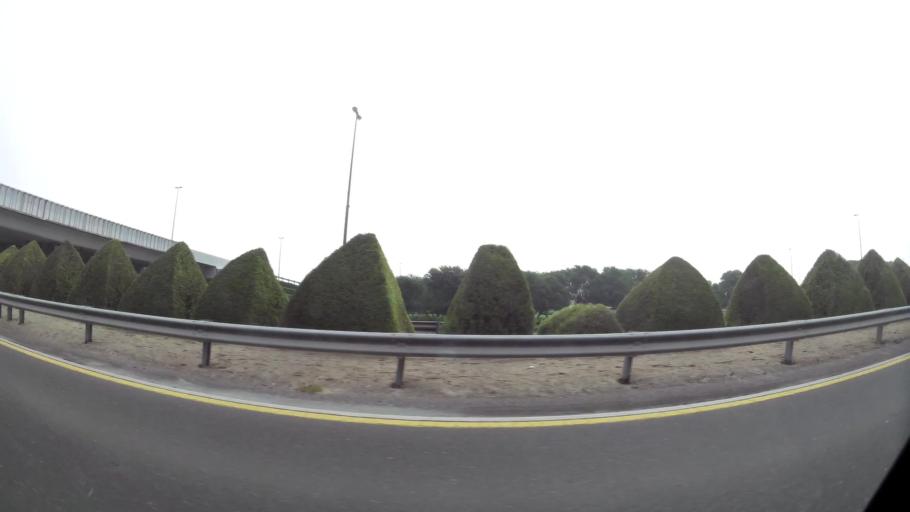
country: AE
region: Dubai
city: Dubai
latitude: 25.1741
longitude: 55.3212
